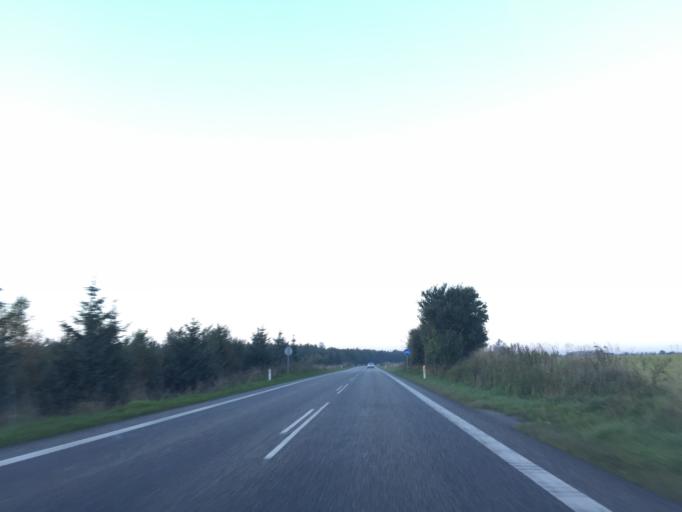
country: DK
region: South Denmark
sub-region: Aabenraa Kommune
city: Lojt Kirkeby
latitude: 55.0889
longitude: 9.4324
